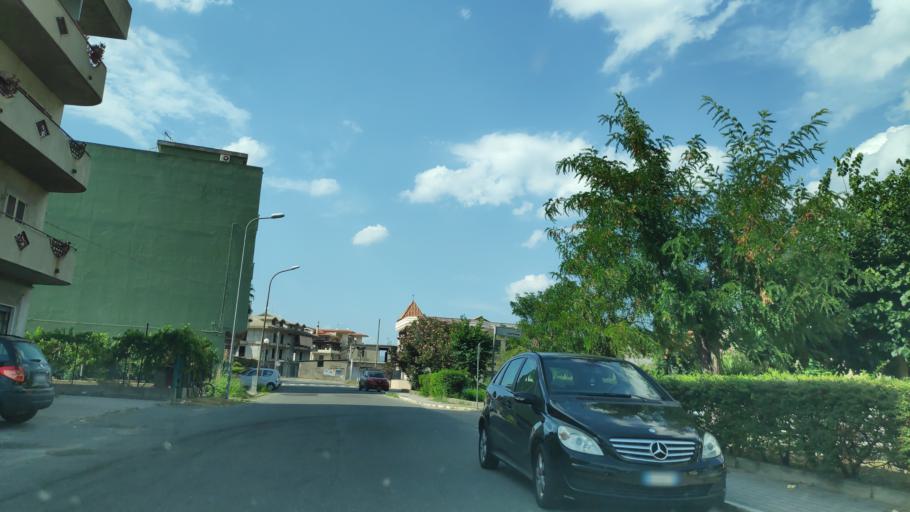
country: IT
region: Calabria
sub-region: Provincia di Catanzaro
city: Marina di Davoli
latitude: 38.6667
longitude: 16.5421
